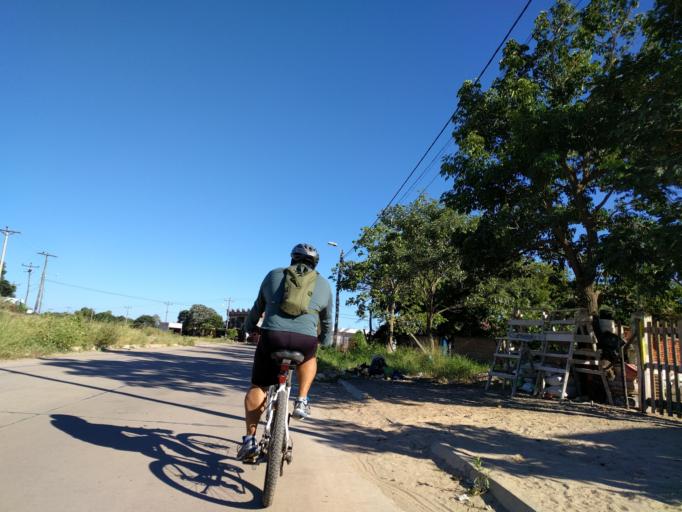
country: BO
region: Santa Cruz
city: Santa Cruz de la Sierra
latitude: -17.8475
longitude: -63.2431
